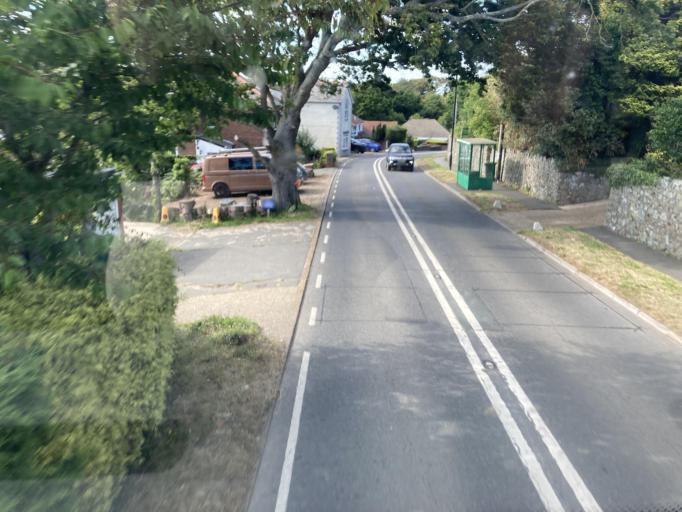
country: GB
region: England
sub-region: Isle of Wight
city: Shanklin
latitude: 50.6285
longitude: -1.1970
